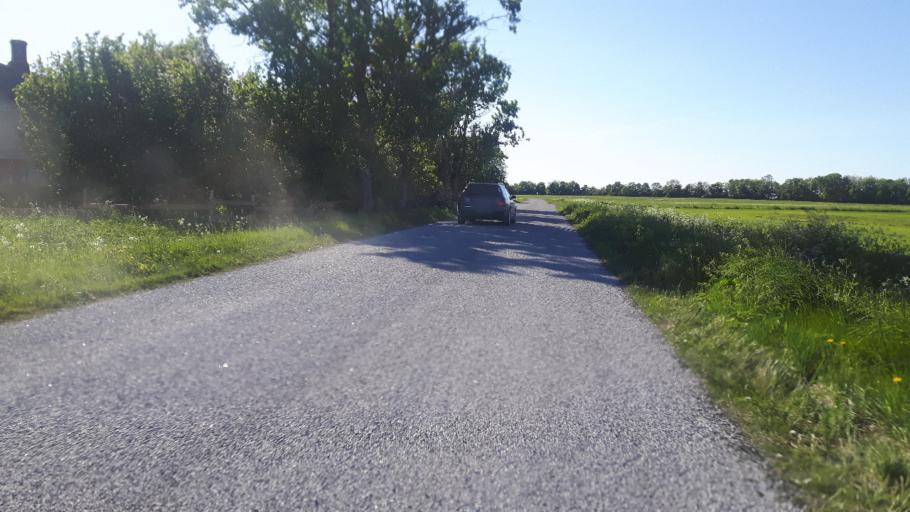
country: EE
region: Ida-Virumaa
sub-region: Kohtla-Jaerve linn
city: Kohtla-Jarve
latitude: 59.4370
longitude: 27.1979
